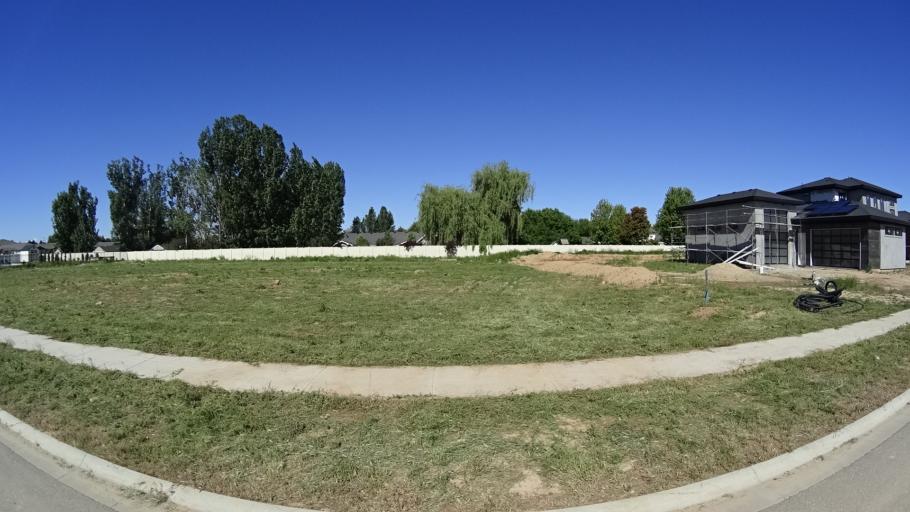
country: US
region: Idaho
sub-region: Ada County
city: Eagle
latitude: 43.6653
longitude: -116.3979
